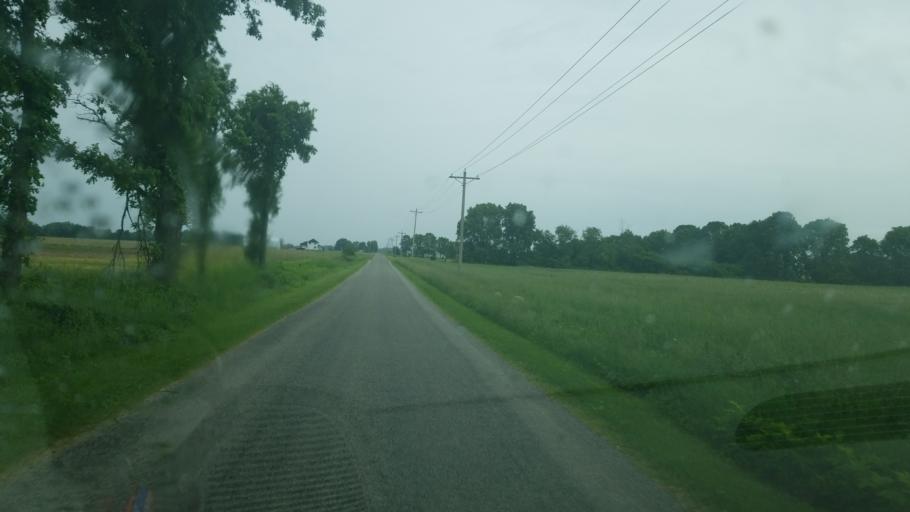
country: US
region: Ohio
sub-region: Marion County
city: Marion
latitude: 40.6599
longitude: -83.0007
